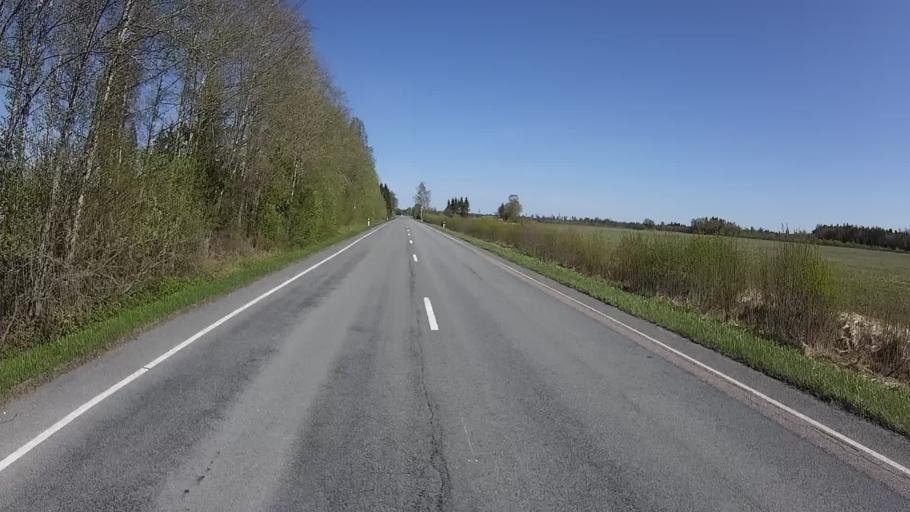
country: EE
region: Raplamaa
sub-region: Jaervakandi vald
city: Jarvakandi
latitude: 58.8319
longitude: 24.7973
